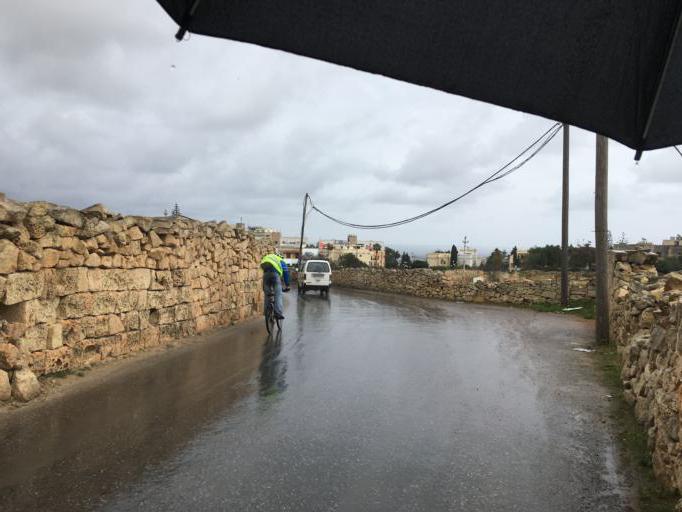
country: MT
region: Is-Swieqi
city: Swieqi
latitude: 35.9177
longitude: 14.4663
